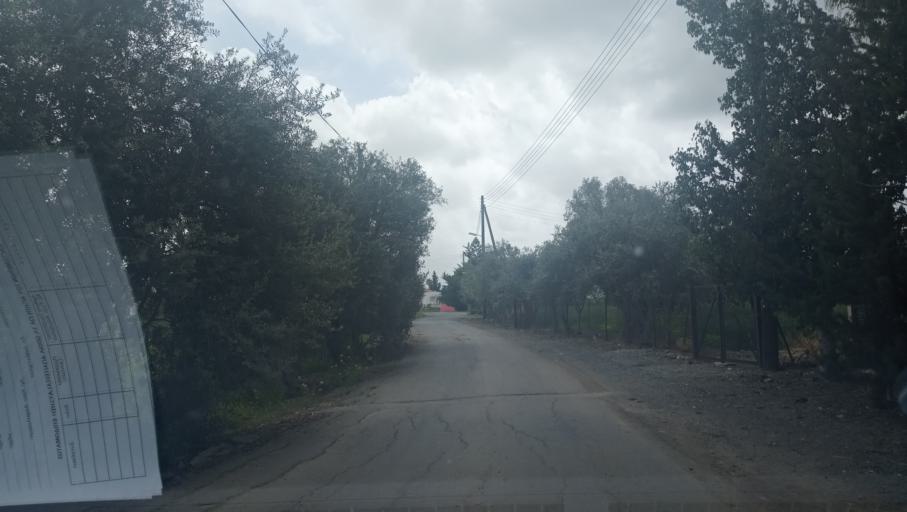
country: CY
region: Lefkosia
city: Pano Deftera
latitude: 35.0796
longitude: 33.2616
